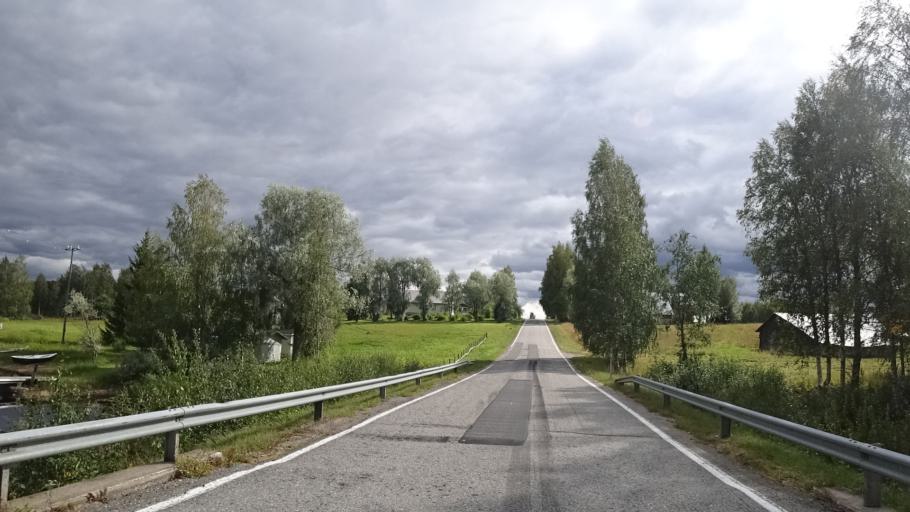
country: FI
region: North Karelia
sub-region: Joensuu
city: Ilomantsi
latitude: 62.4519
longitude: 31.1148
